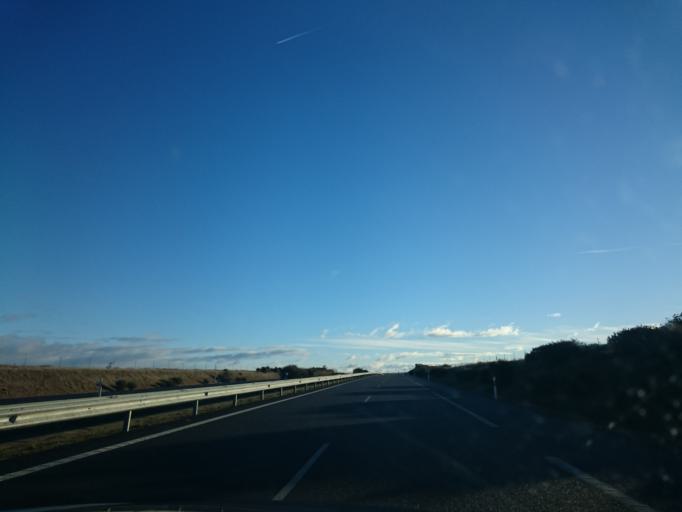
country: ES
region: Castille and Leon
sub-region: Provincia de Leon
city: Villamoratiel de las Matas
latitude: 42.4206
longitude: -5.2612
